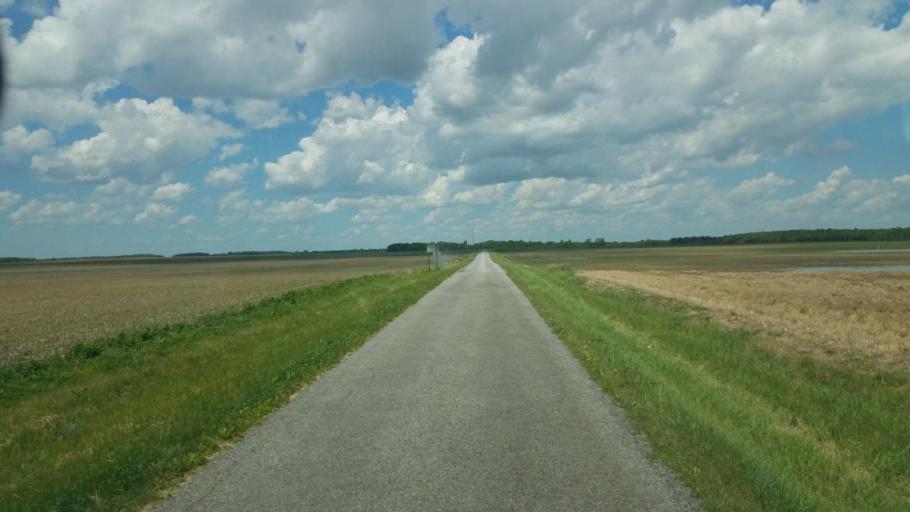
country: US
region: Ohio
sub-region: Wyandot County
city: Upper Sandusky
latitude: 40.7522
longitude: -83.2409
